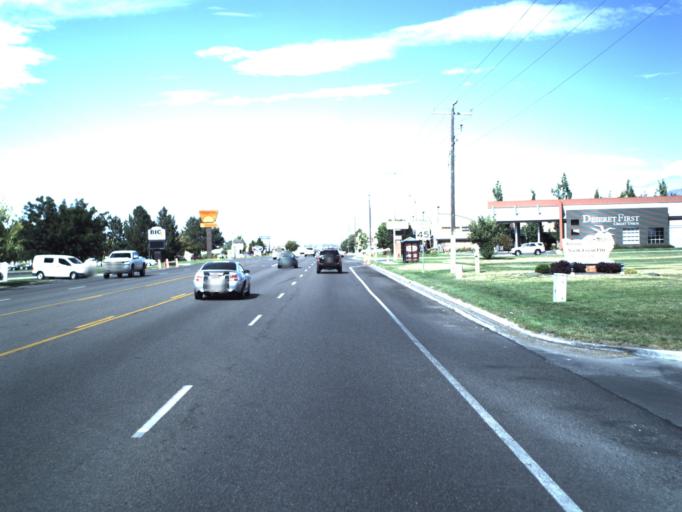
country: US
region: Utah
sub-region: Cache County
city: Logan
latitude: 41.7602
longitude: -111.8342
